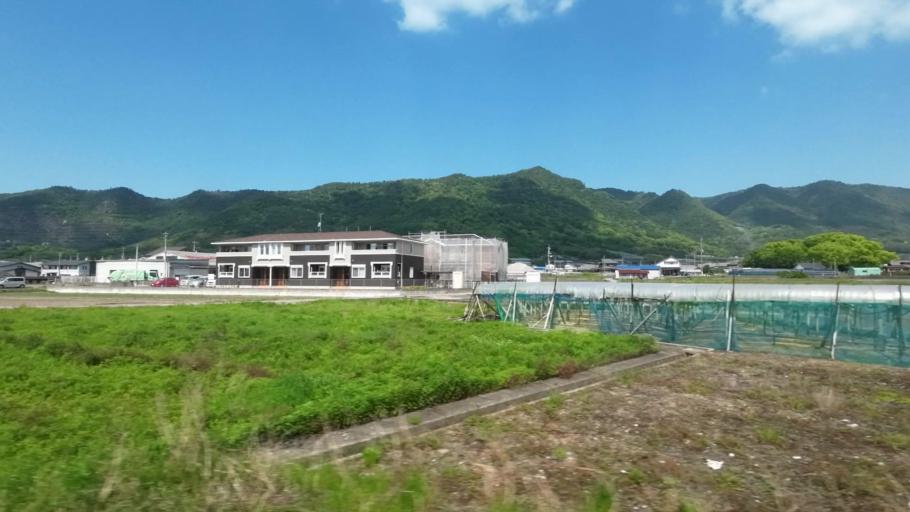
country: JP
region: Kagawa
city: Kan'onjicho
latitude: 34.1548
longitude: 133.6880
